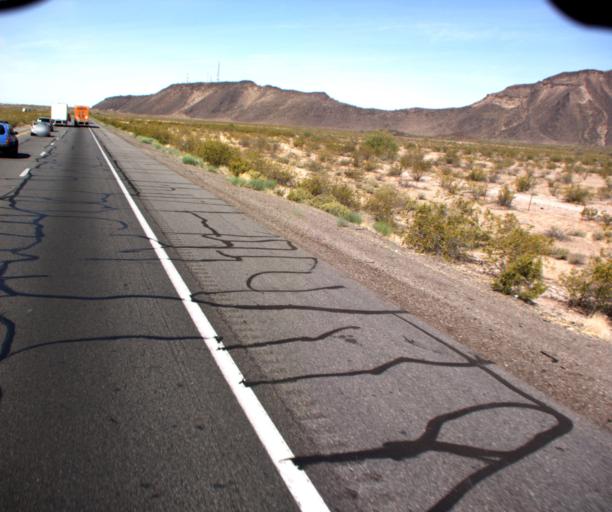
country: US
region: Arizona
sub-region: Maricopa County
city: Buckeye
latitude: 33.5237
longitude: -113.0864
